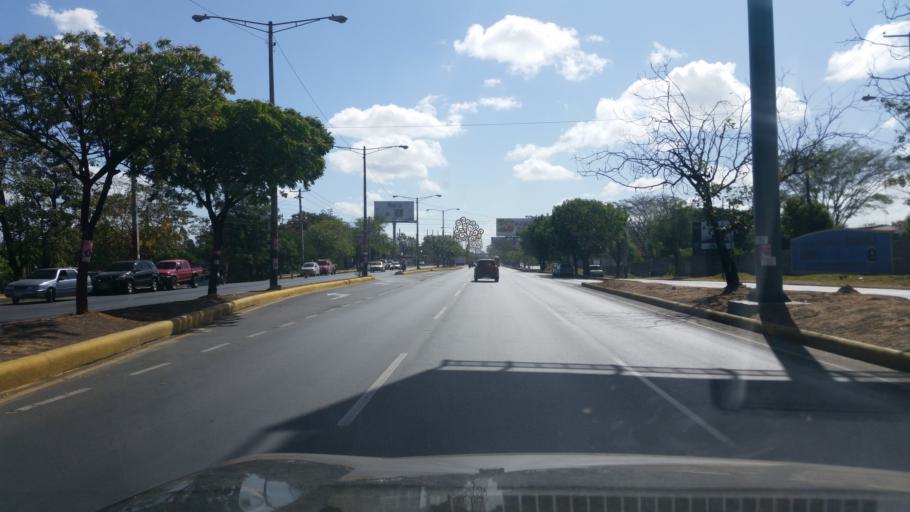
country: NI
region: Managua
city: Managua
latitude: 12.1489
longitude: -86.2059
